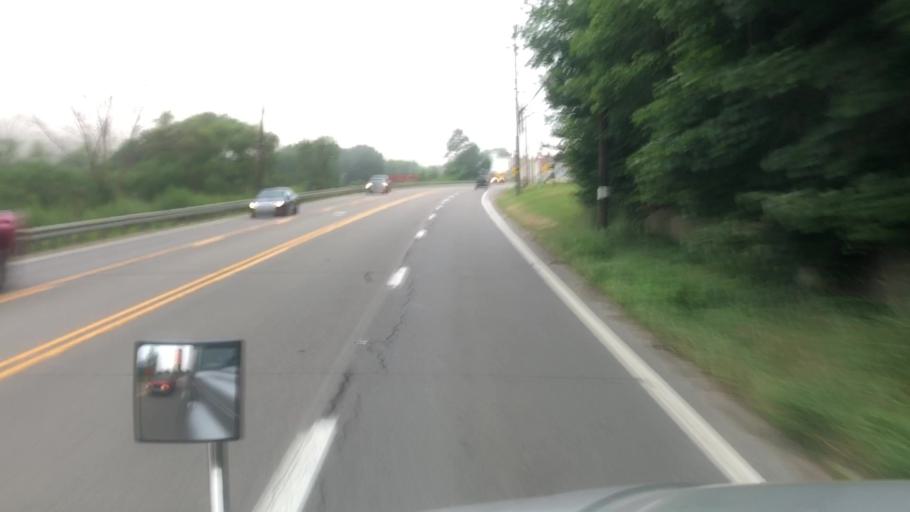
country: US
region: Pennsylvania
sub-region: Venango County
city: Woodland Heights
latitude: 41.4071
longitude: -79.7472
